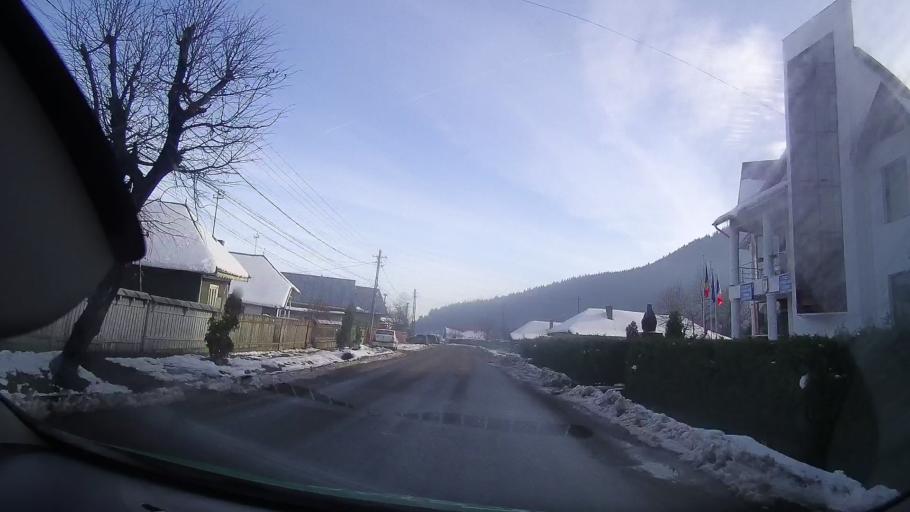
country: RO
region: Neamt
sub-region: Comuna Garcina
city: Garcina
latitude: 46.9764
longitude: 26.3511
